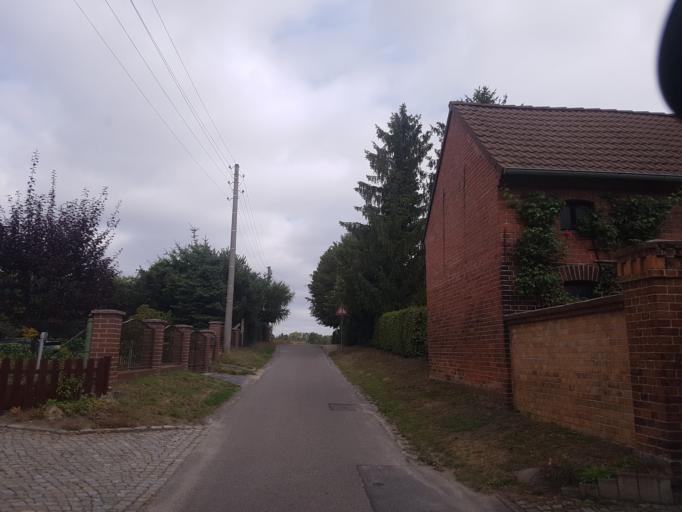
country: DE
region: Brandenburg
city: Calau
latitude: 51.7242
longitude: 13.9499
